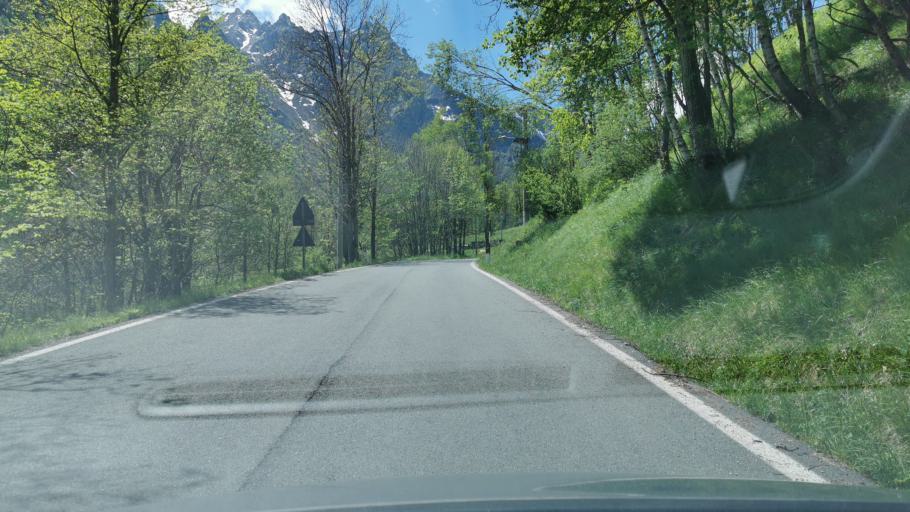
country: IT
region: Piedmont
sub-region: Provincia di Torino
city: Usseglio
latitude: 45.2240
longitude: 7.1967
